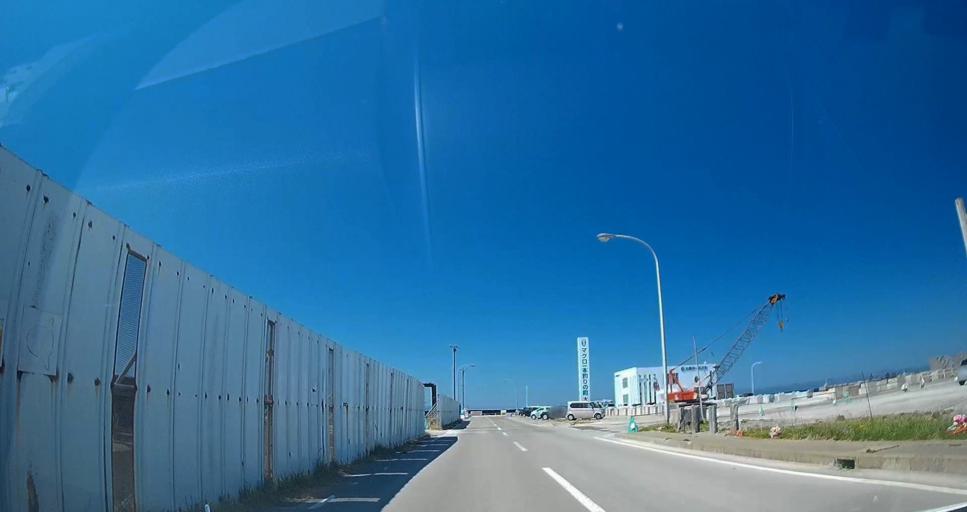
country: JP
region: Hokkaido
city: Hakodate
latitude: 41.5249
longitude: 140.8992
